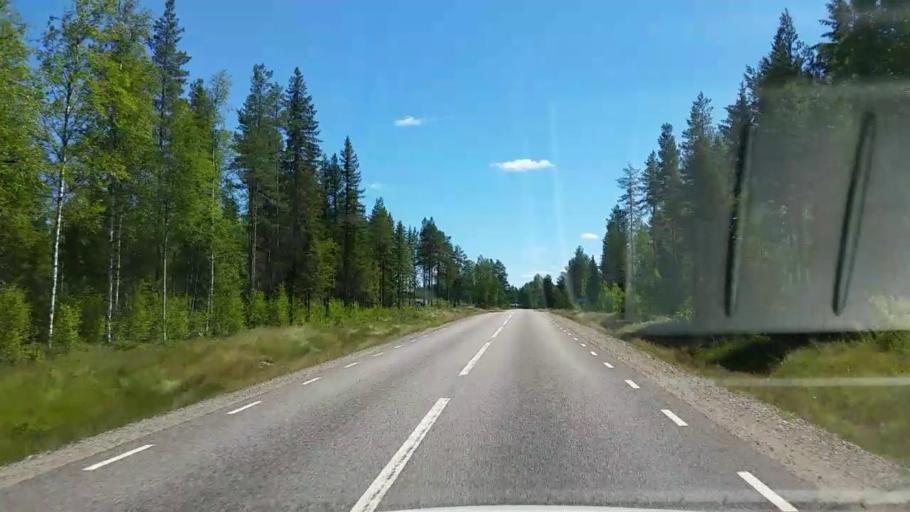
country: SE
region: Gaevleborg
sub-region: Ovanakers Kommun
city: Edsbyn
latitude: 61.4566
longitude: 15.7036
